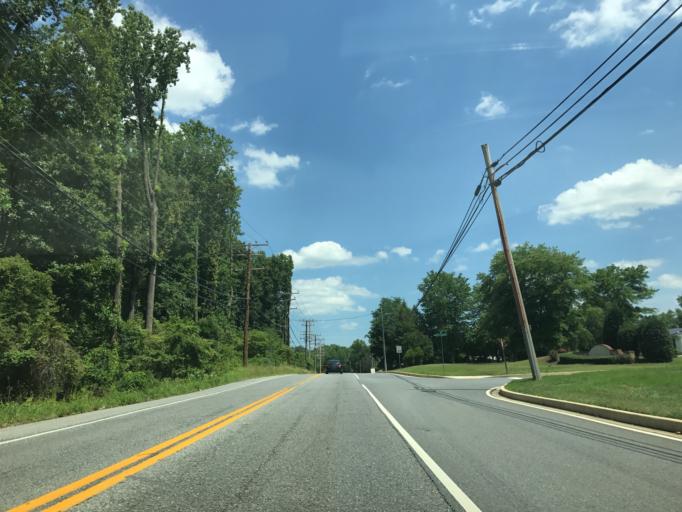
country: US
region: Maryland
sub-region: Prince George's County
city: Bowie
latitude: 38.9701
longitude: -76.7622
